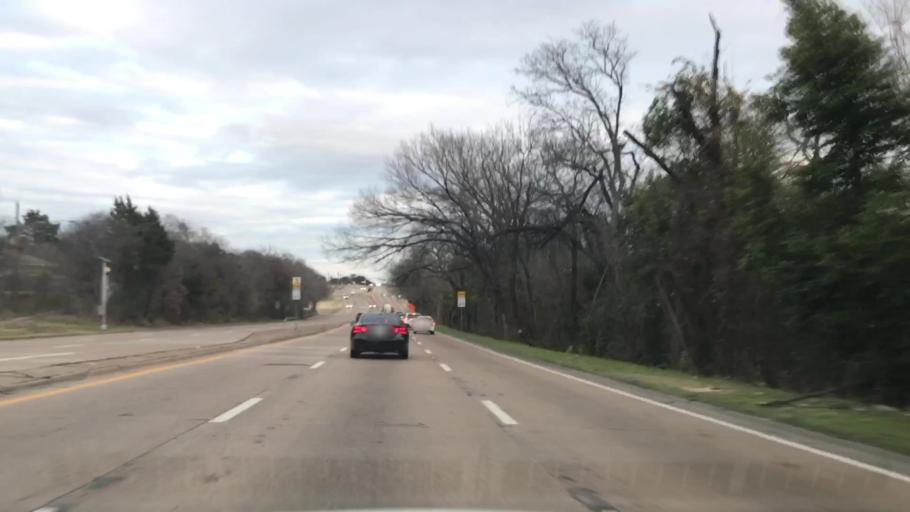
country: US
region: Texas
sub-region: Dallas County
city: Cockrell Hill
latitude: 32.6911
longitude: -96.8518
